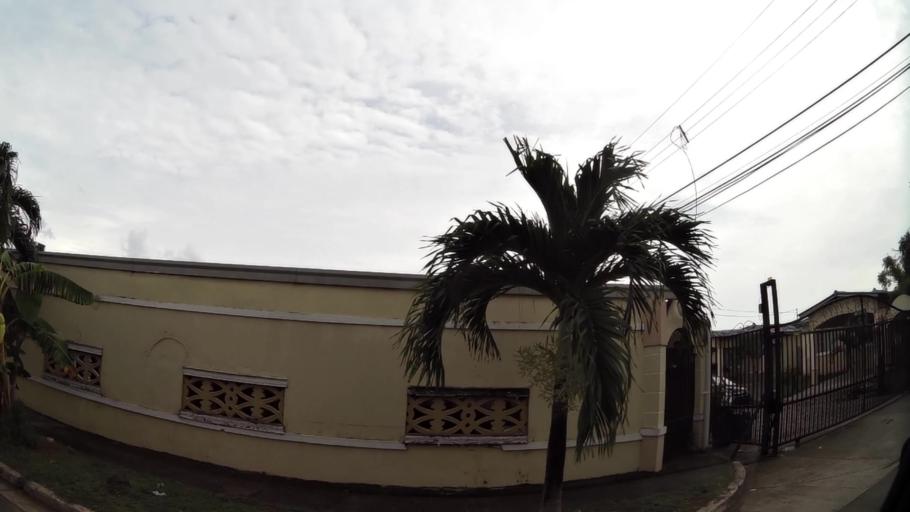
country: PA
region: Panama
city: Tocumen
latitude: 9.0438
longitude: -79.4038
